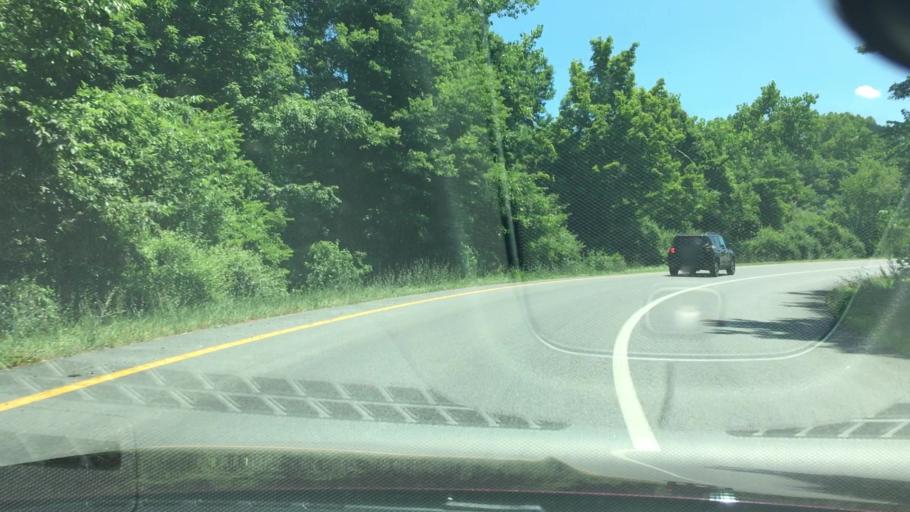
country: US
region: New York
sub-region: Putnam County
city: Brewster
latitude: 41.3980
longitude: -73.5955
